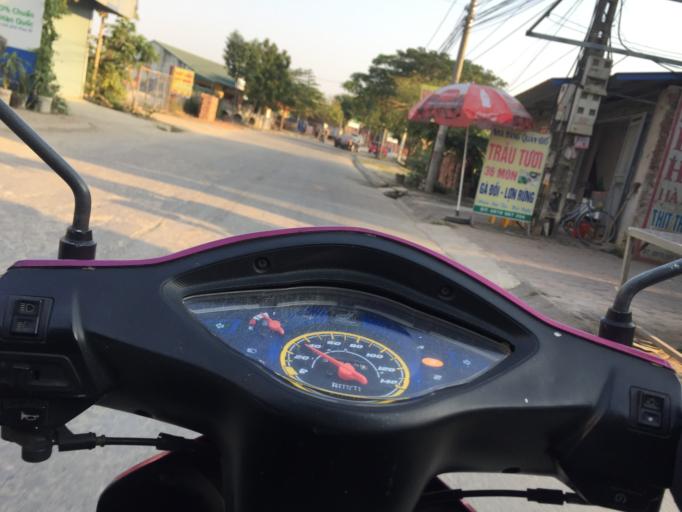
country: VN
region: Ha Noi
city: Chuc Son
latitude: 20.9189
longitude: 105.7136
